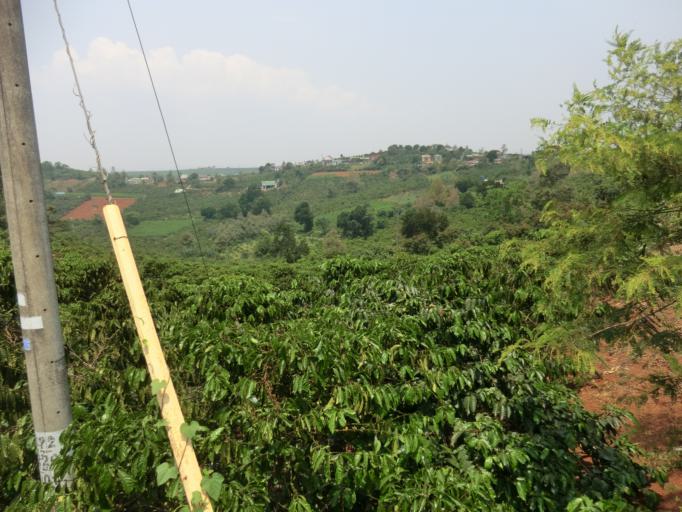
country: VN
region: Lam Dong
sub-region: Thanh Pho Bao Loc
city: Bao Loc
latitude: 11.5913
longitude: 107.7871
